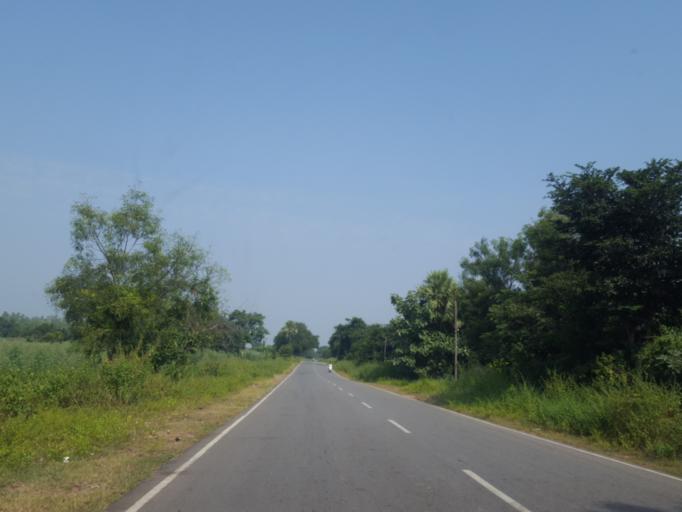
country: IN
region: Telangana
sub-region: Khammam
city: Yellandu
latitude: 17.6178
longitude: 80.3091
